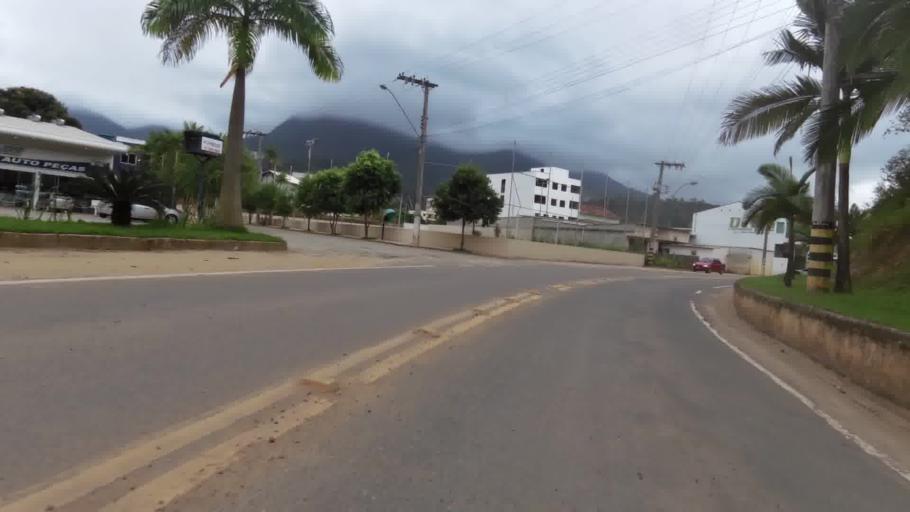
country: BR
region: Espirito Santo
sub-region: Alfredo Chaves
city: Alfredo Chaves
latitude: -20.6412
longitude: -40.7467
